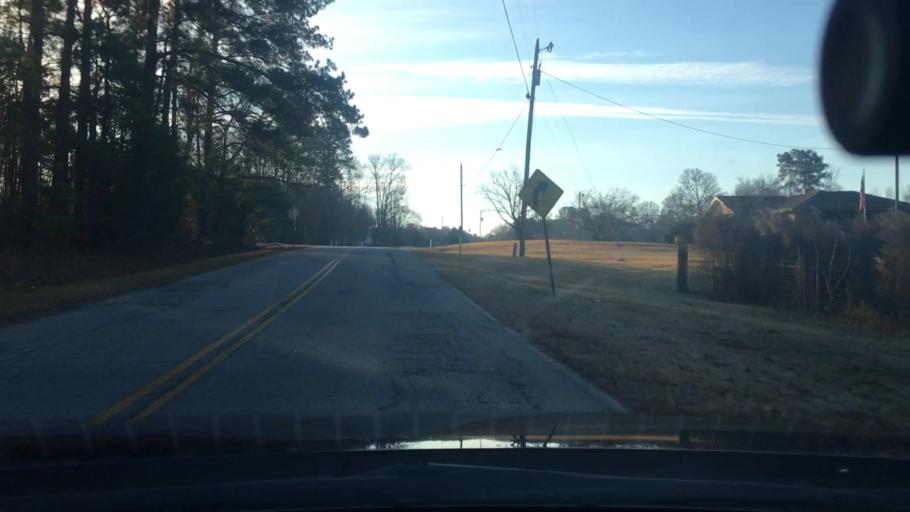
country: US
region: Georgia
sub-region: Spalding County
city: Experiment
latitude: 33.2722
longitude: -84.3145
